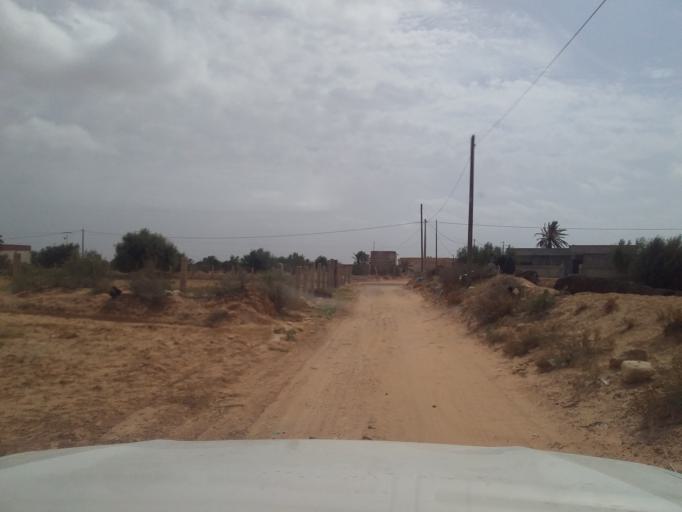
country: TN
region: Qabis
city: Matmata
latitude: 33.6181
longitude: 10.2631
